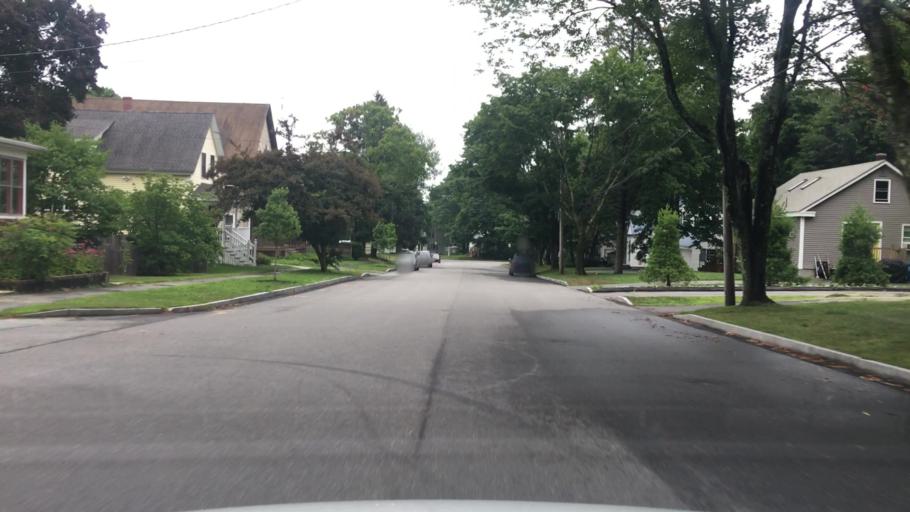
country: US
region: Maine
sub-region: Cumberland County
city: Portland
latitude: 43.6862
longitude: -70.2667
